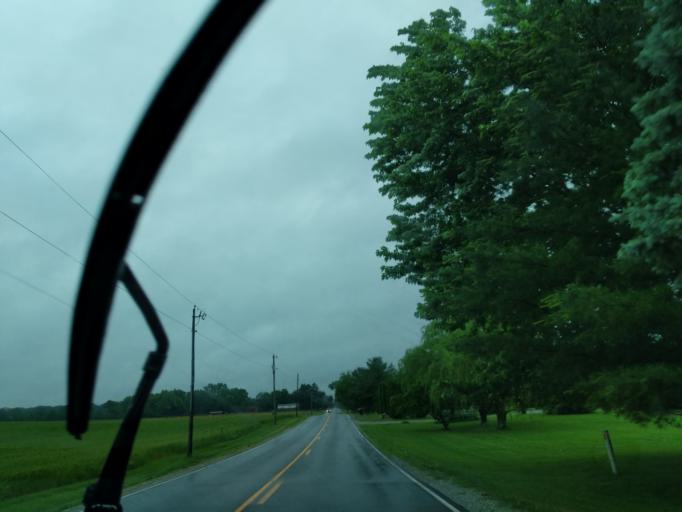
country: US
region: Indiana
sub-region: Hamilton County
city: Noblesville
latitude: 40.0662
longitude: -85.9411
